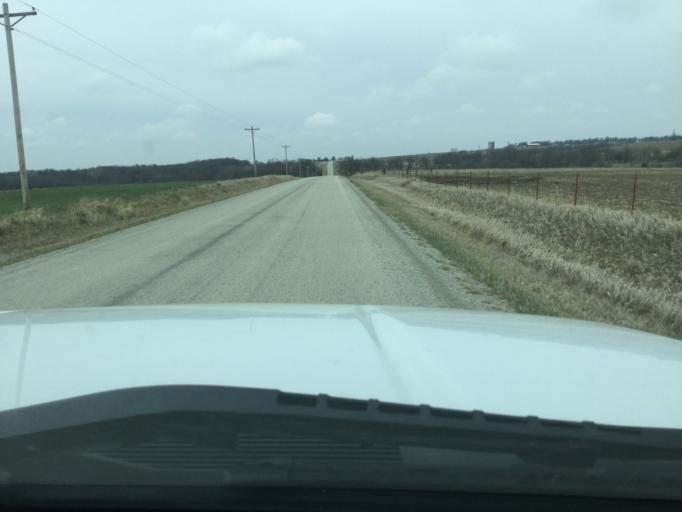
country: US
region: Kansas
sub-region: Nemaha County
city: Sabetha
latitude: 39.8603
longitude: -95.7142
